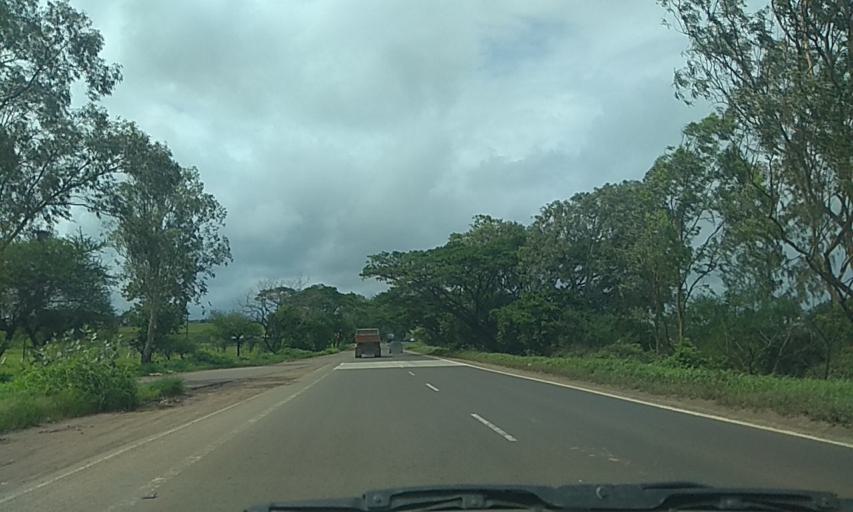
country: IN
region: Maharashtra
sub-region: Kolhapur
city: Kolhapur
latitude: 16.6553
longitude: 74.2682
